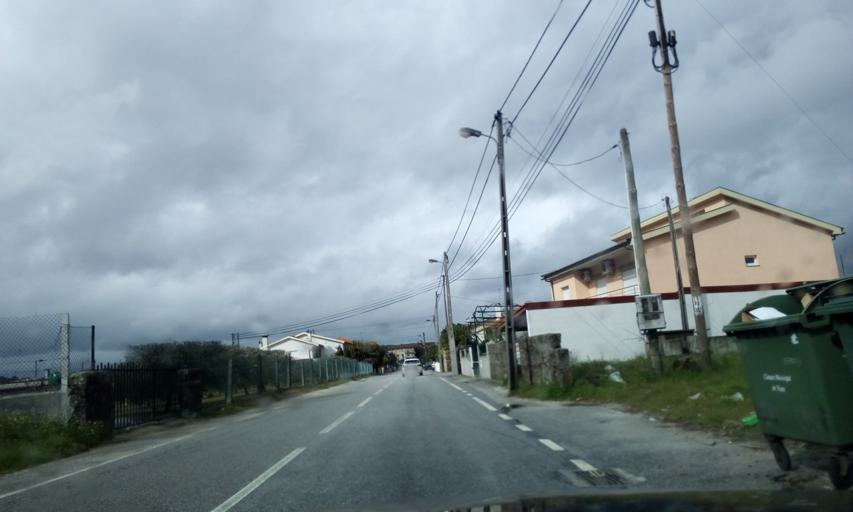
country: PT
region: Viseu
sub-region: Viseu
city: Rio de Loba
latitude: 40.6410
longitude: -7.8662
